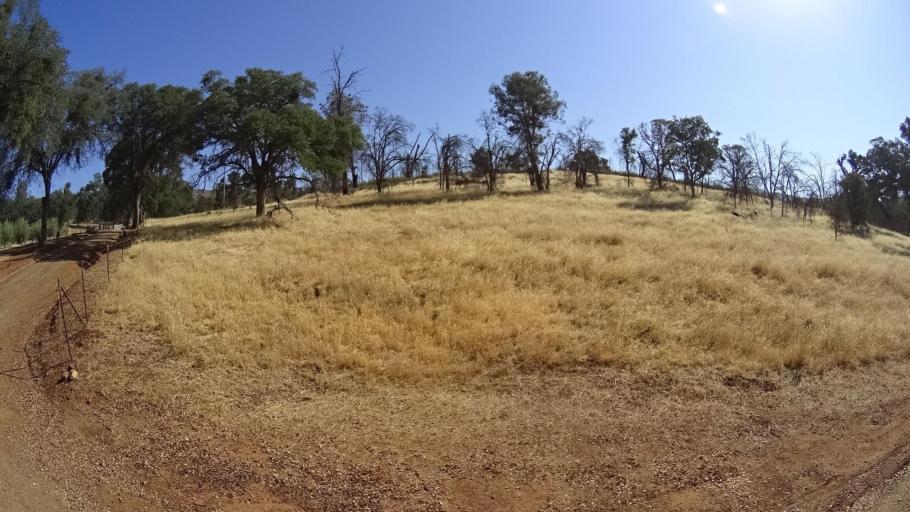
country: US
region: California
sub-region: Mariposa County
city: Mariposa
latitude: 37.6173
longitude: -120.2331
